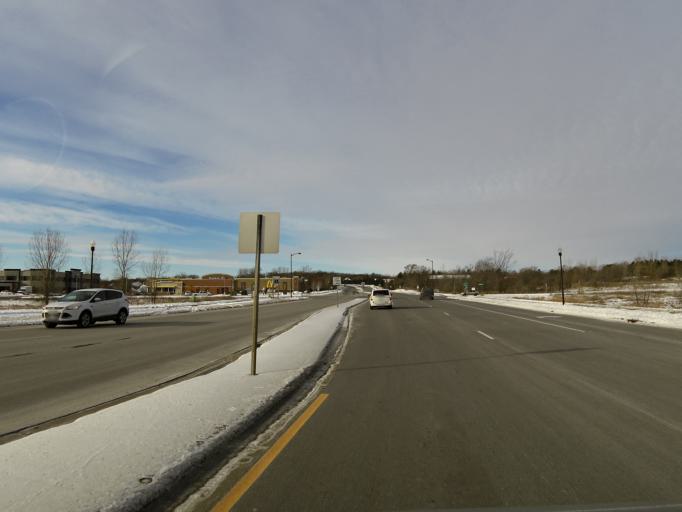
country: US
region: Minnesota
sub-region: Dakota County
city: Burnsville
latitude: 44.7149
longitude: -93.2868
